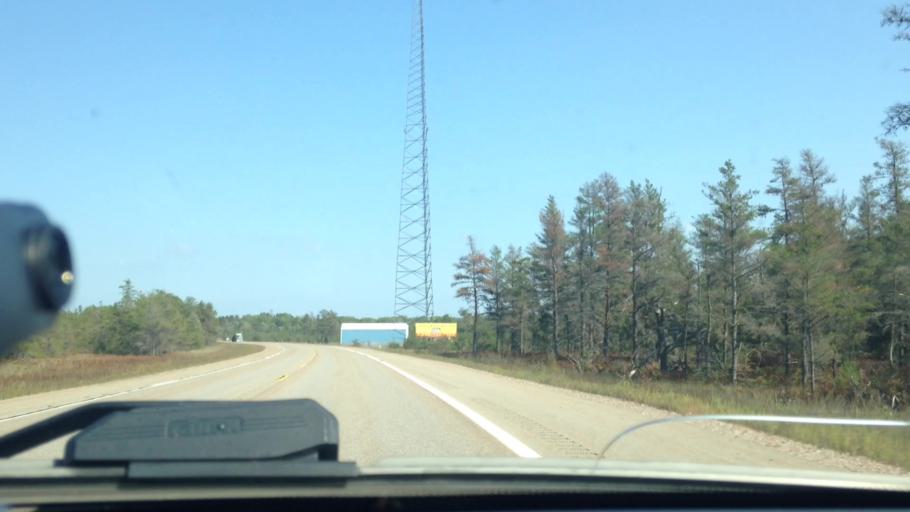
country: US
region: Michigan
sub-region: Chippewa County
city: Sault Ste. Marie
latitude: 46.3589
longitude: -84.7944
